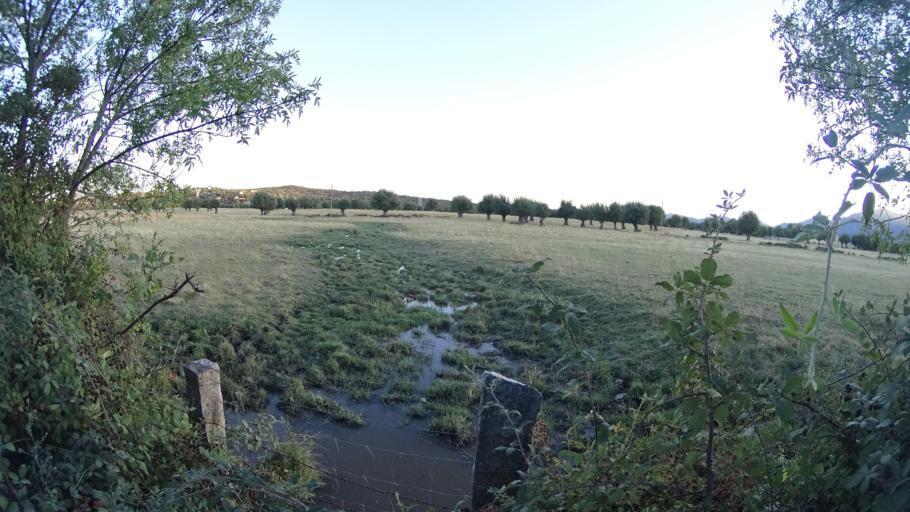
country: ES
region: Madrid
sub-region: Provincia de Madrid
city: Navalquejigo
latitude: 40.6373
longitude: -4.0468
